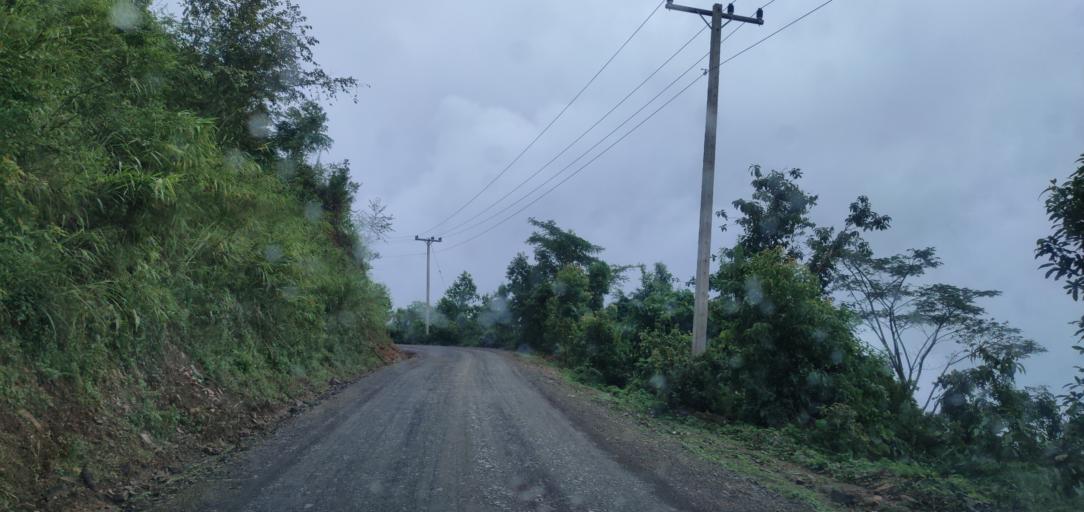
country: LA
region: Phongsali
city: Phongsali
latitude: 21.4370
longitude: 102.1615
